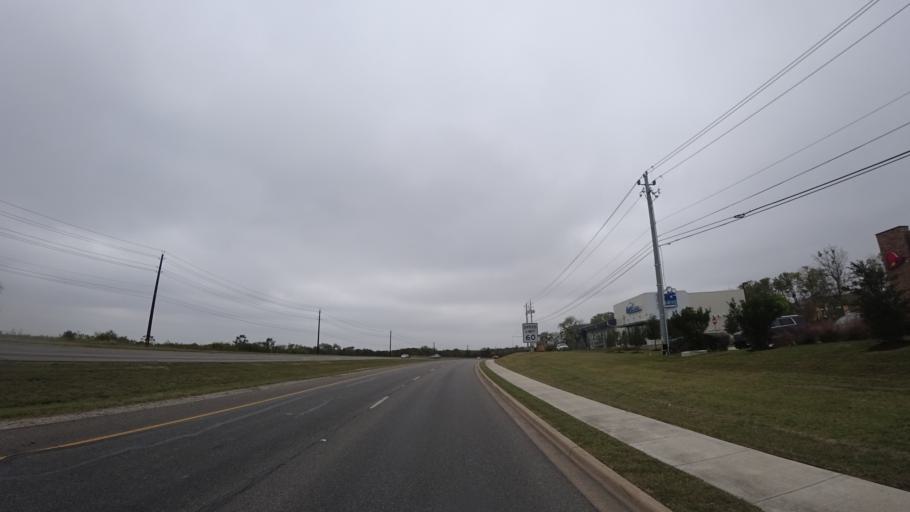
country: US
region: Texas
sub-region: Travis County
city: Pflugerville
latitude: 30.3887
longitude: -97.6510
